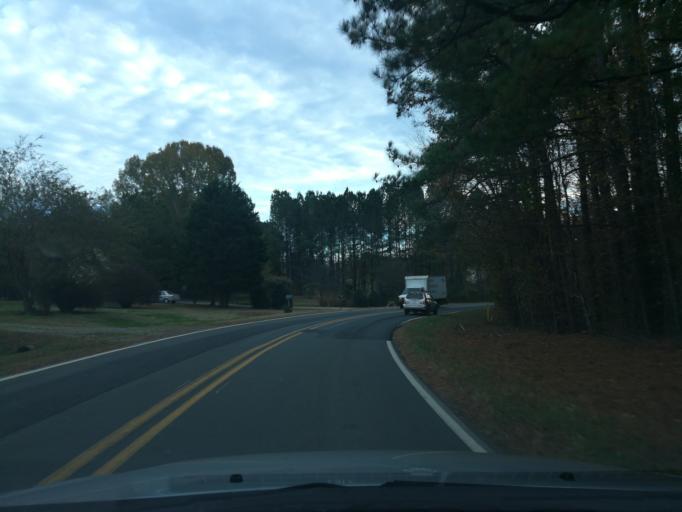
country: US
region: North Carolina
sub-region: Orange County
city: Carrboro
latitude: 35.9809
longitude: -79.0774
